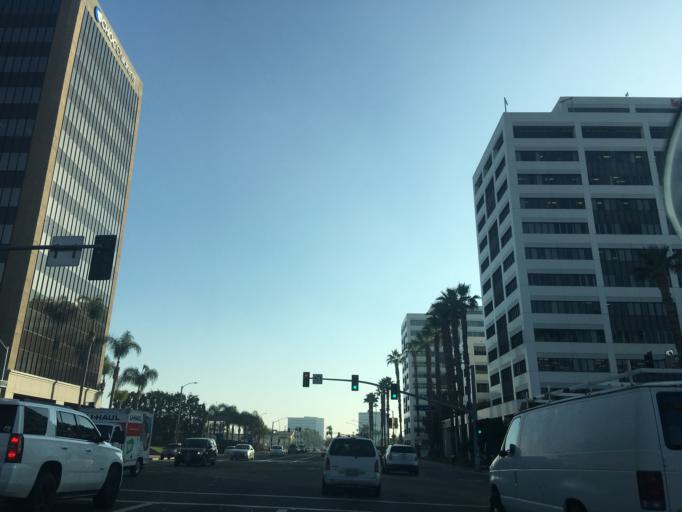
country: US
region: California
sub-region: Orange County
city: Orange
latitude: 33.7808
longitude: -117.8675
